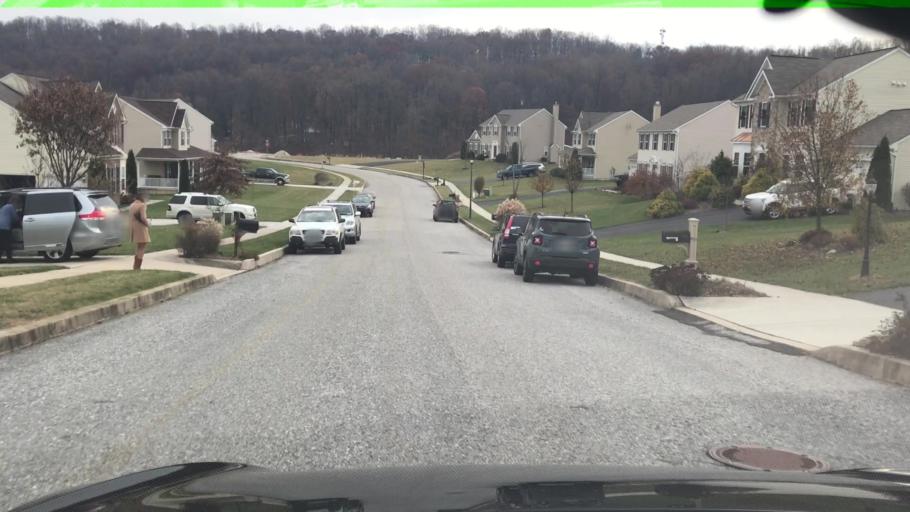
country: US
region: Pennsylvania
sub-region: Cumberland County
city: New Cumberland
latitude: 40.1882
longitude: -76.8659
